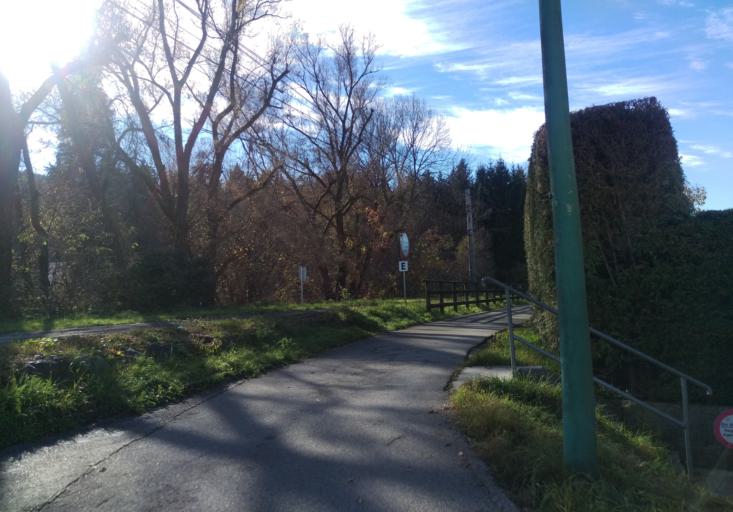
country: AT
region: Styria
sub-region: Graz Stadt
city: Mariatrost
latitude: 47.1014
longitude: 15.4838
